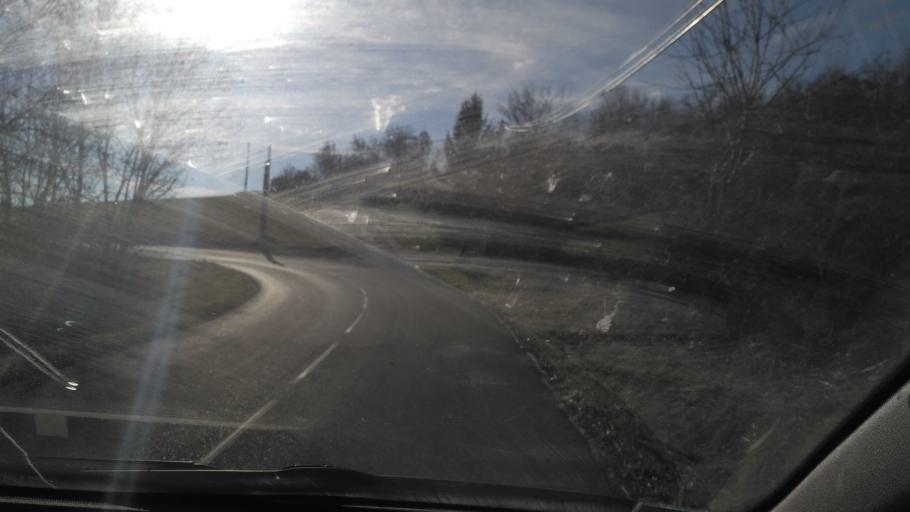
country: FR
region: Rhone-Alpes
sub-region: Departement de l'Isere
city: Saint-Antoine-l'Abbaye
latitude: 45.1716
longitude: 5.2006
